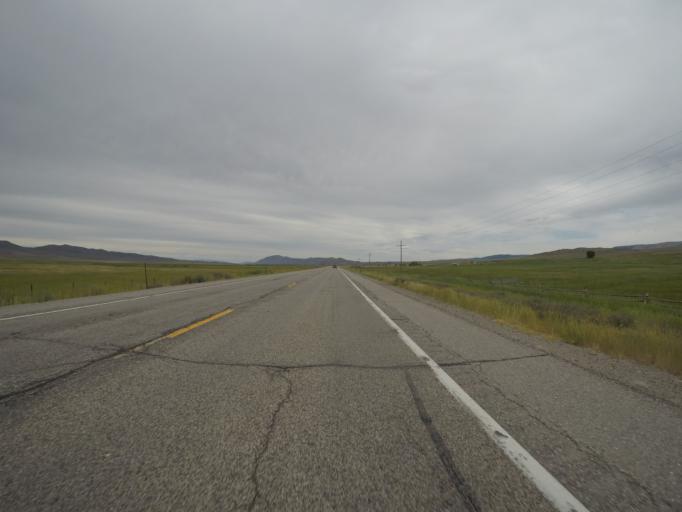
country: US
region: Utah
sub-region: Rich County
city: Randolph
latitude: 42.0107
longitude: -110.9372
